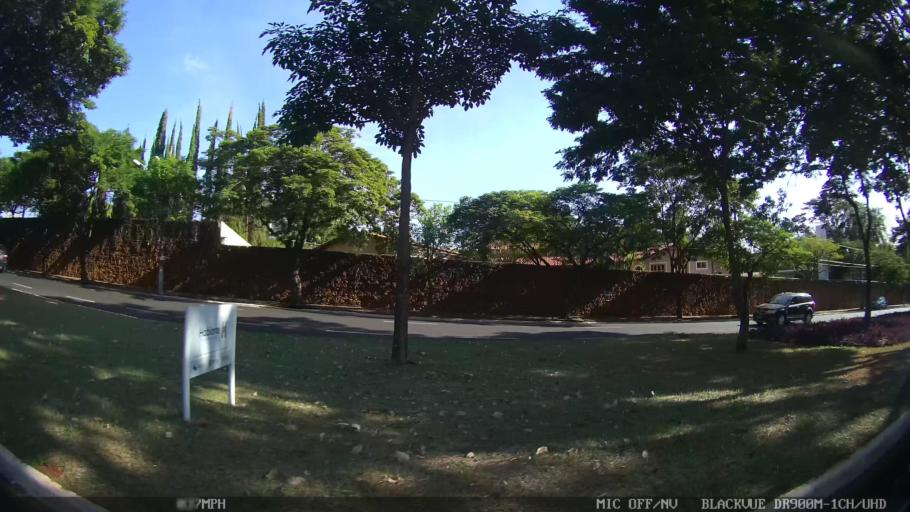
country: BR
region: Sao Paulo
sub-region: Ribeirao Preto
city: Ribeirao Preto
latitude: -21.1985
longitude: -47.7926
